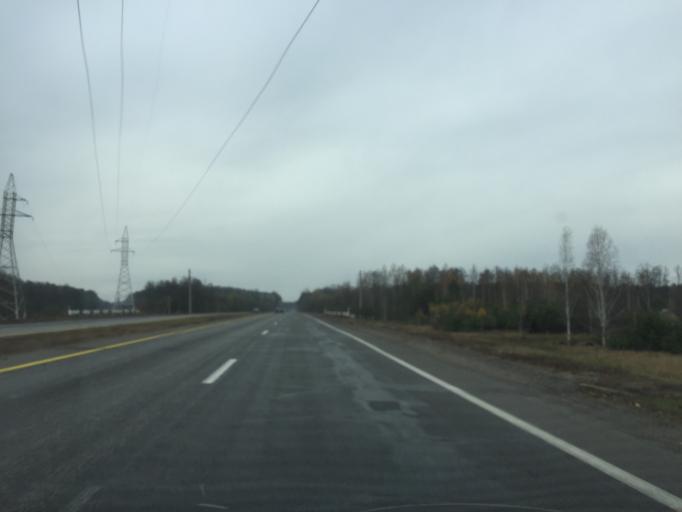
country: BY
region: Gomel
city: Horad Rechytsa
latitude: 52.3576
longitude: 30.6800
